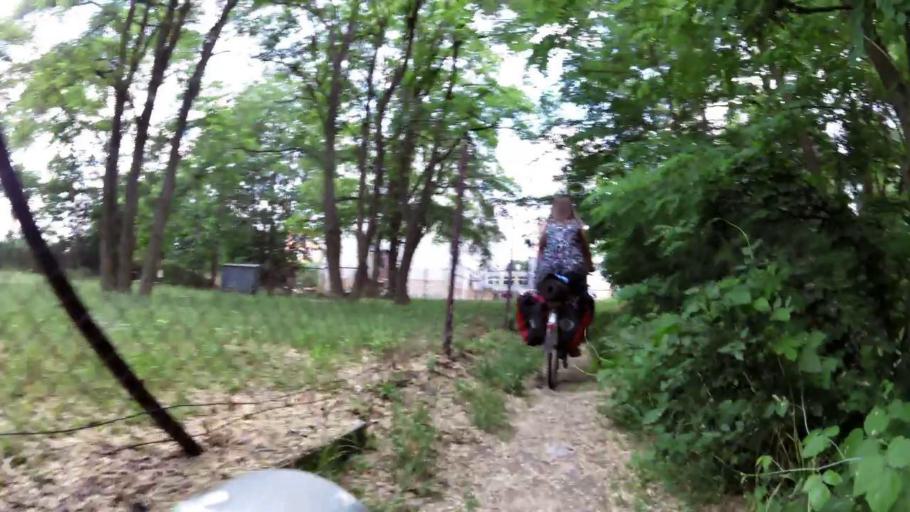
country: PL
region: Kujawsko-Pomorskie
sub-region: Bydgoszcz
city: Fordon
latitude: 53.1440
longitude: 18.1601
